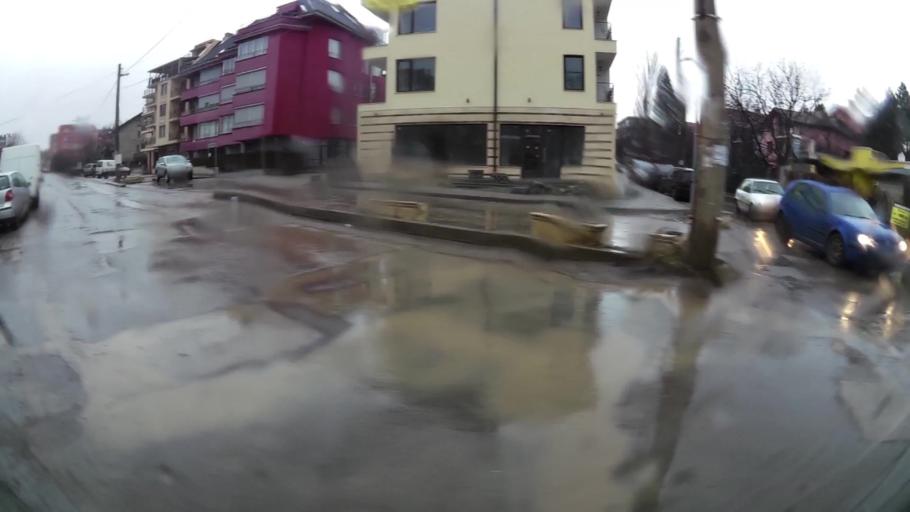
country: BG
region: Sofia-Capital
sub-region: Stolichna Obshtina
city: Sofia
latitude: 42.6454
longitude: 23.3334
